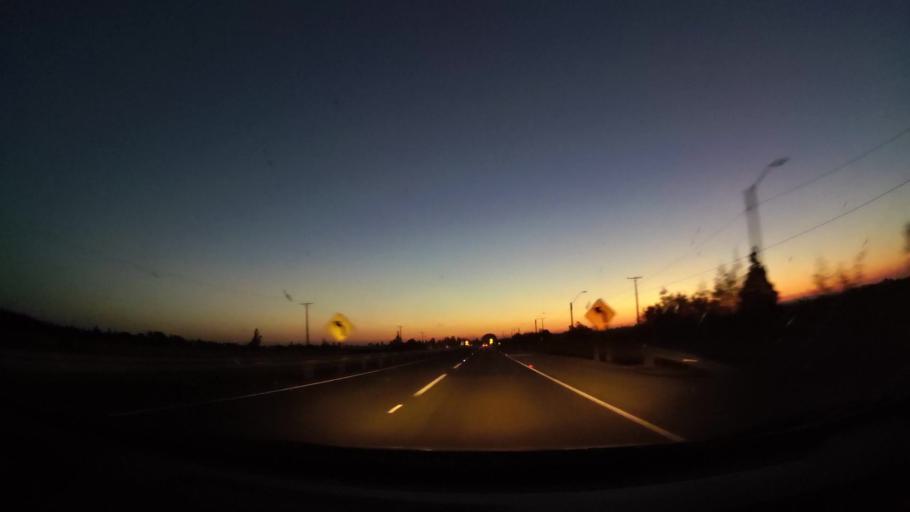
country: CL
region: Biobio
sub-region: Provincia de Nuble
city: San Carlos
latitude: -36.4004
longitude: -71.9397
